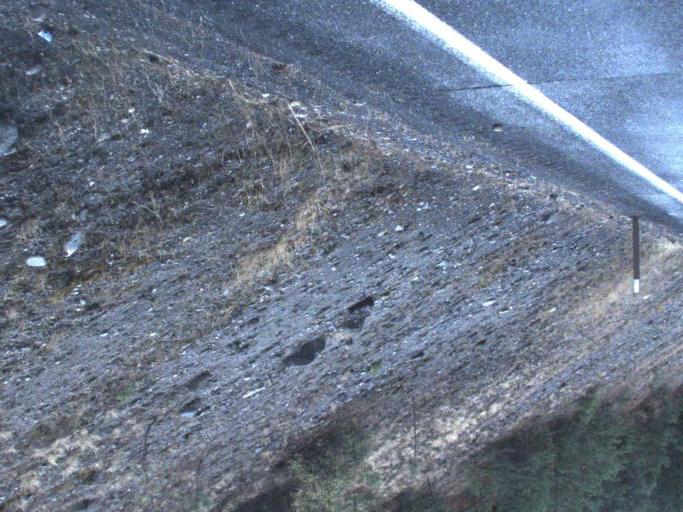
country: US
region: Washington
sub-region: Spokane County
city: Fairchild Air Force Base
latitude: 47.8378
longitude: -117.8595
